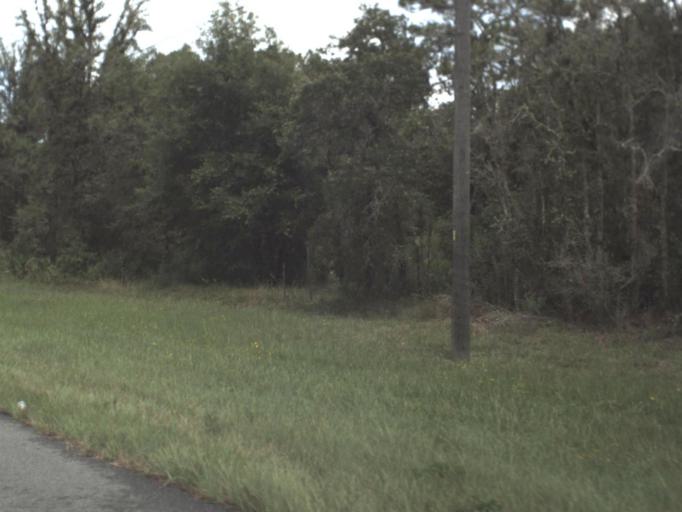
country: US
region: Florida
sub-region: Hernando County
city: Ridge Manor
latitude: 28.5452
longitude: -82.1613
